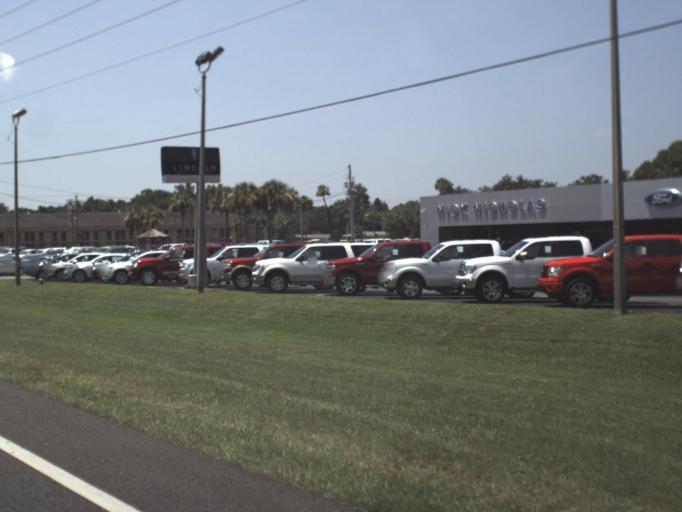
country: US
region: Florida
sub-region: Citrus County
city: Crystal River
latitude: 28.9210
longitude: -82.6112
